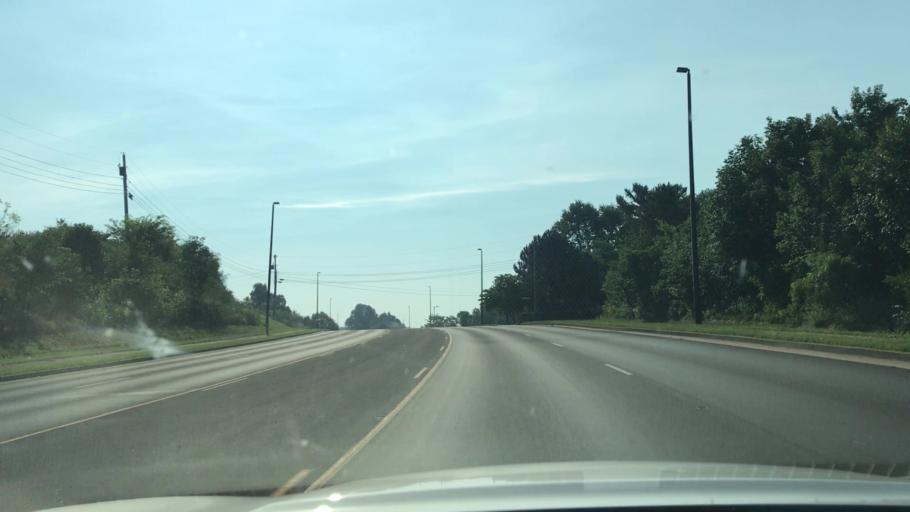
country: US
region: Kentucky
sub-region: Barren County
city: Glasgow
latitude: 37.0102
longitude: -85.9464
